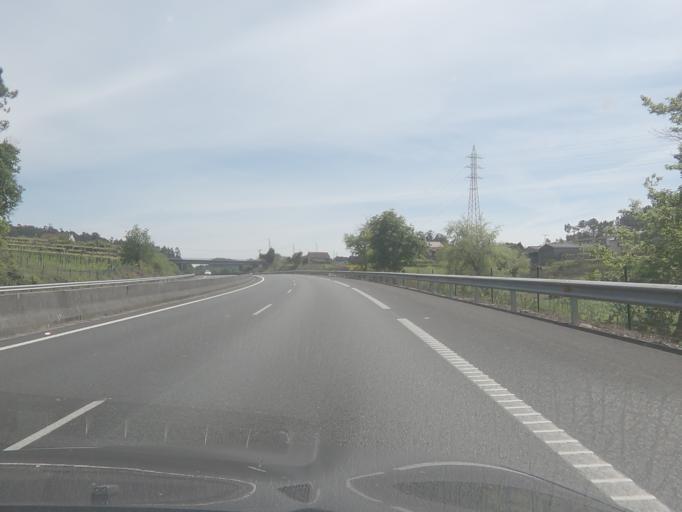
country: ES
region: Galicia
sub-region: Provincia de Pontevedra
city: Valga
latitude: 42.6699
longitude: -8.6336
